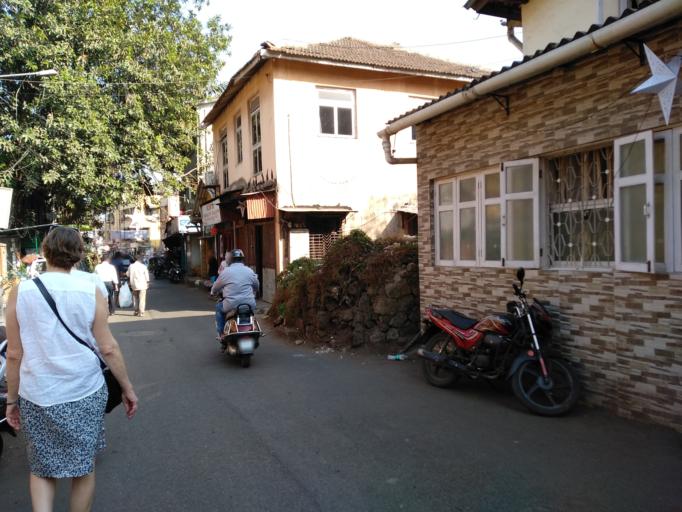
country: IN
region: Maharashtra
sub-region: Mumbai Suburban
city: Mumbai
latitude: 19.0538
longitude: 72.8302
